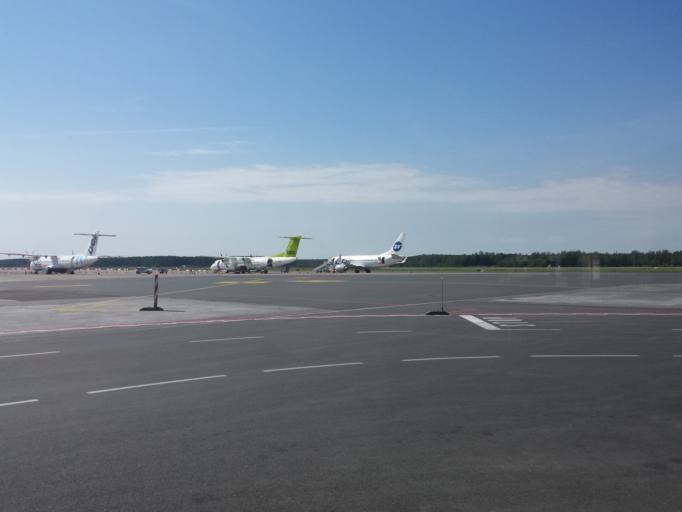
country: LV
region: Babite
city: Pinki
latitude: 56.9217
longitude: 23.9783
